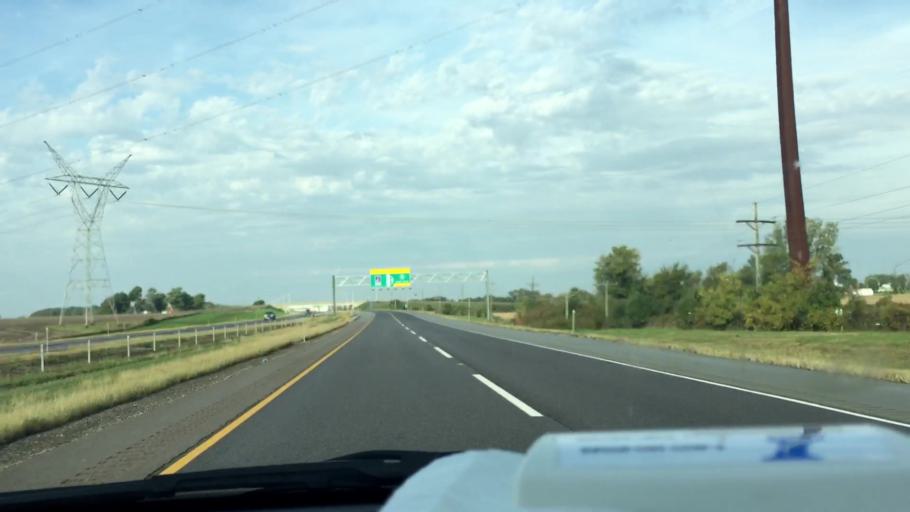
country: US
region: Illinois
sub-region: Lee County
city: Dixon
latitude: 41.8234
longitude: -89.4117
